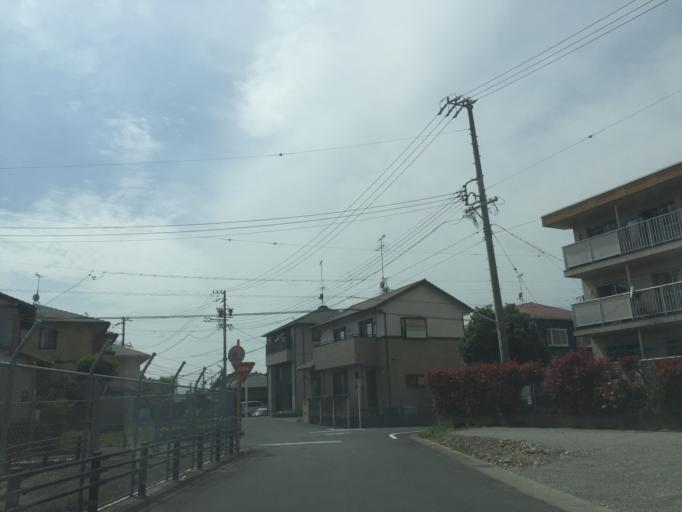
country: JP
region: Shizuoka
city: Kakegawa
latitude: 34.7785
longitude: 138.0273
